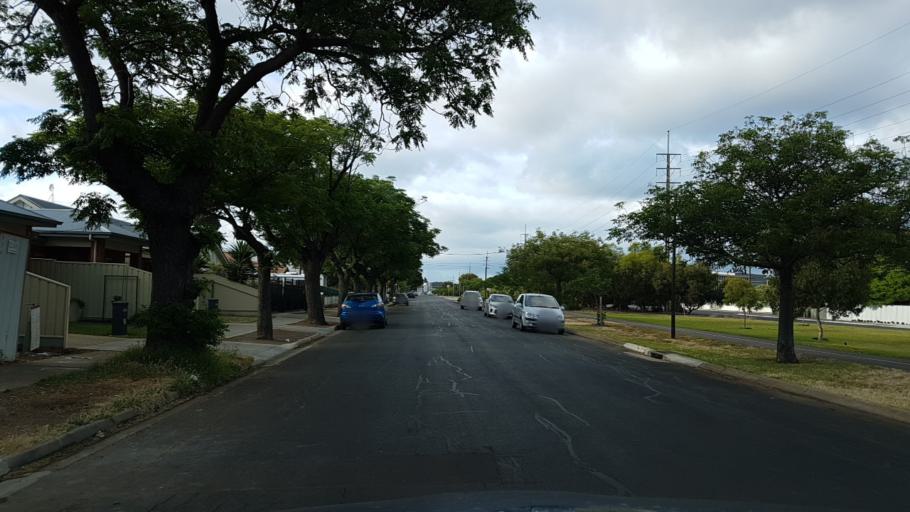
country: AU
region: South Australia
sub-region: Unley
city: Forestville
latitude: -34.9437
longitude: 138.5669
